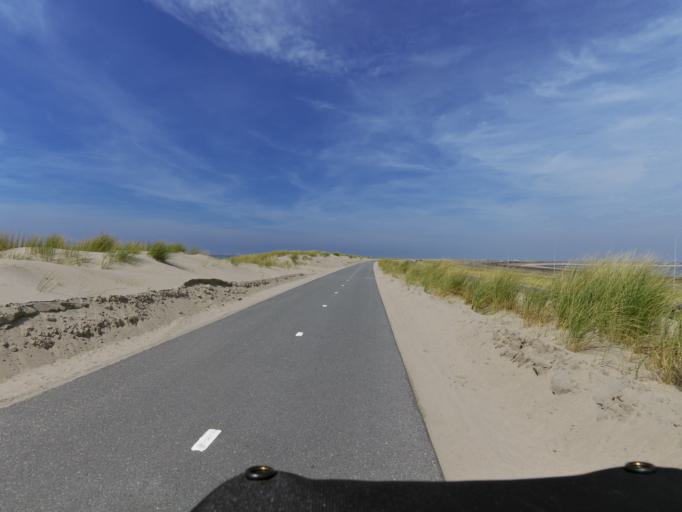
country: NL
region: South Holland
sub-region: Gemeente Goeree-Overflakkee
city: Goedereede
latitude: 51.9589
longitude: 3.9636
